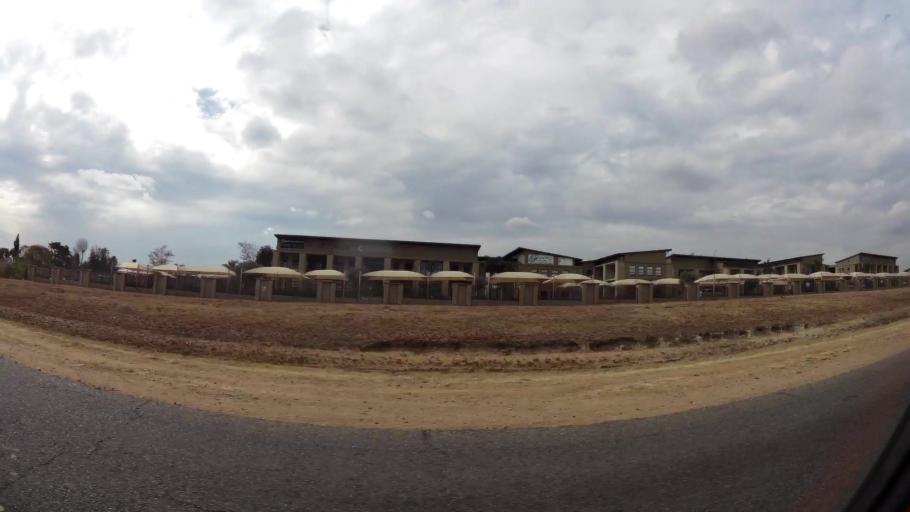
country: ZA
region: Gauteng
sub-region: West Rand District Municipality
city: Muldersdriseloop
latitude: -26.0661
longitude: 27.8476
